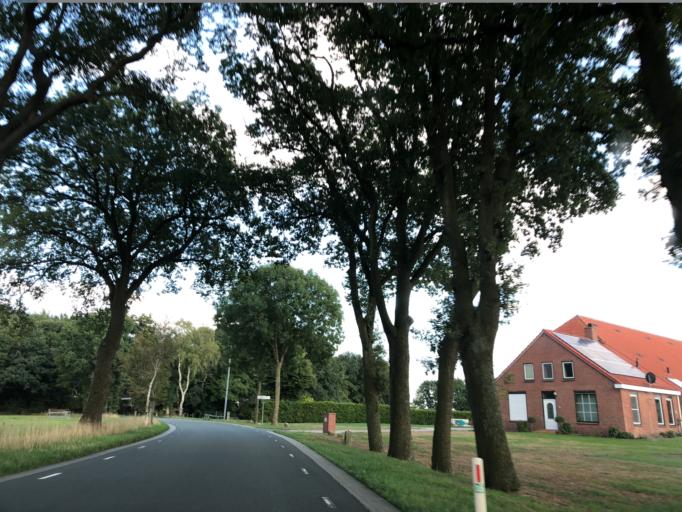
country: DE
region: Lower Saxony
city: Rhede
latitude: 53.0064
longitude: 7.2128
